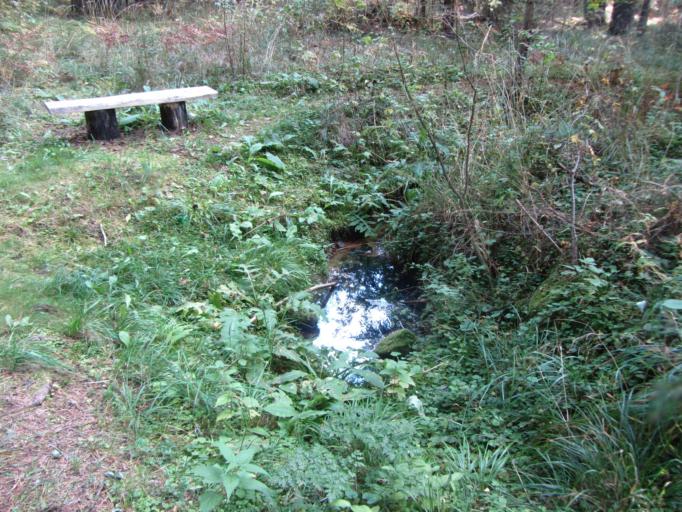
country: LT
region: Panevezys
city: Rokiskis
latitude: 55.7755
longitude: 25.8308
